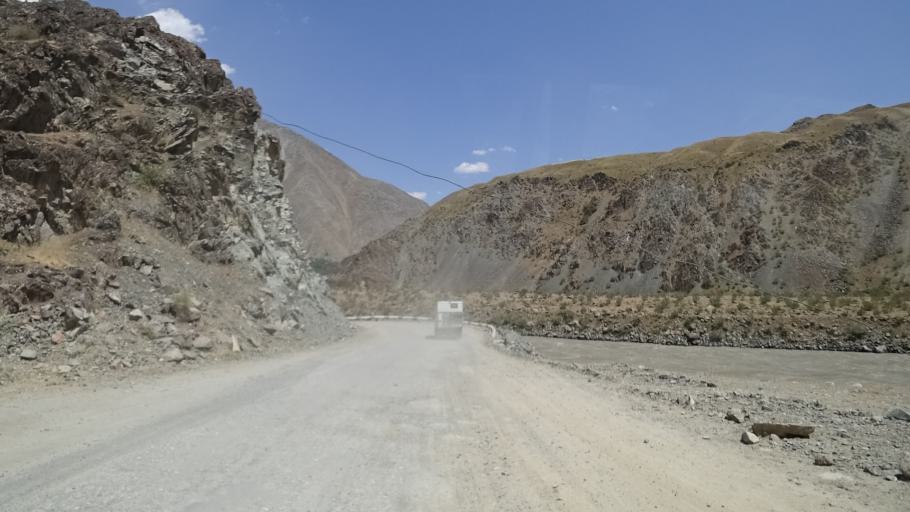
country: AF
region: Badakhshan
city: Nusay
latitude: 38.4642
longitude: 70.8656
